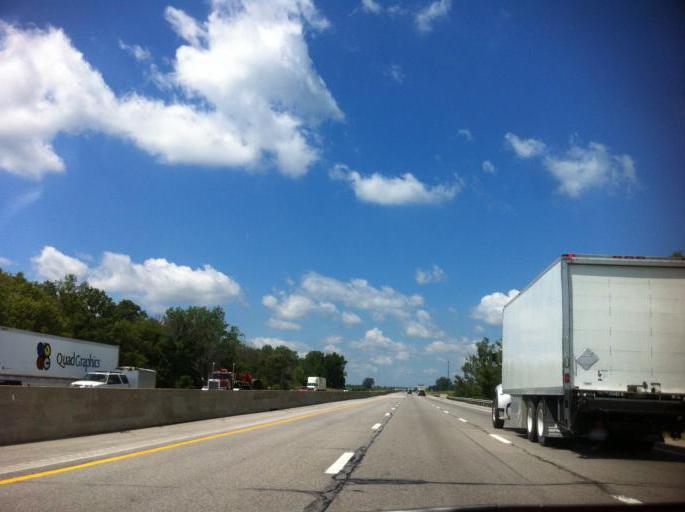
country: US
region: Ohio
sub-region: Sandusky County
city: Stony Prairie
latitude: 41.4255
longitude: -83.1863
